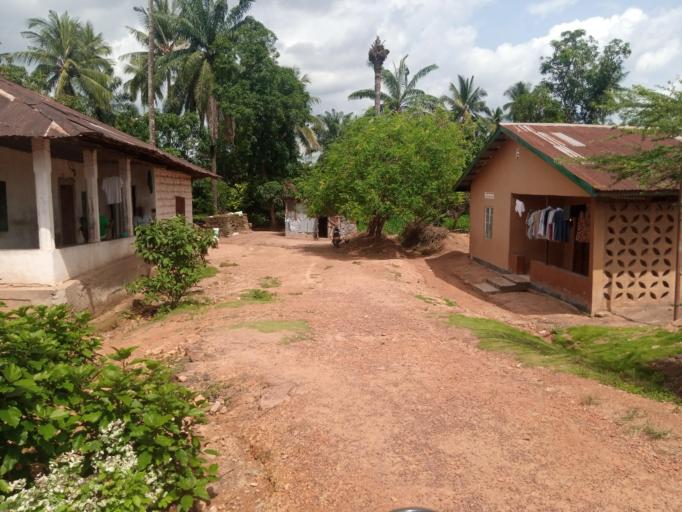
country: SL
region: Southern Province
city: Bo
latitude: 7.9739
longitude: -11.7376
